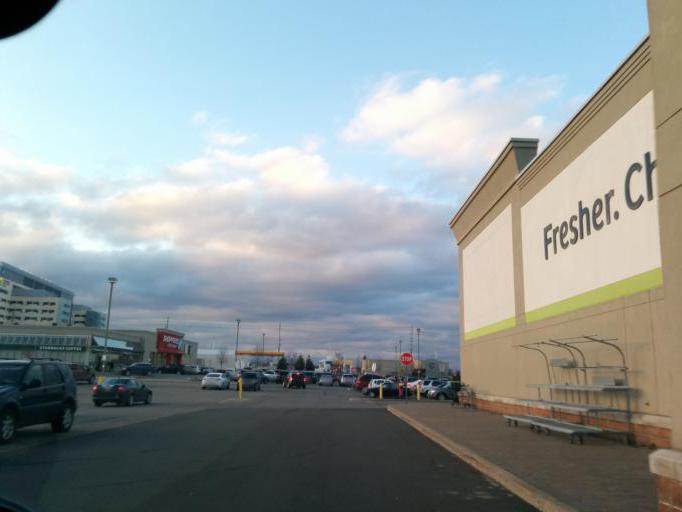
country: CA
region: Ontario
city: Oakville
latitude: 43.4493
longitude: -79.7579
